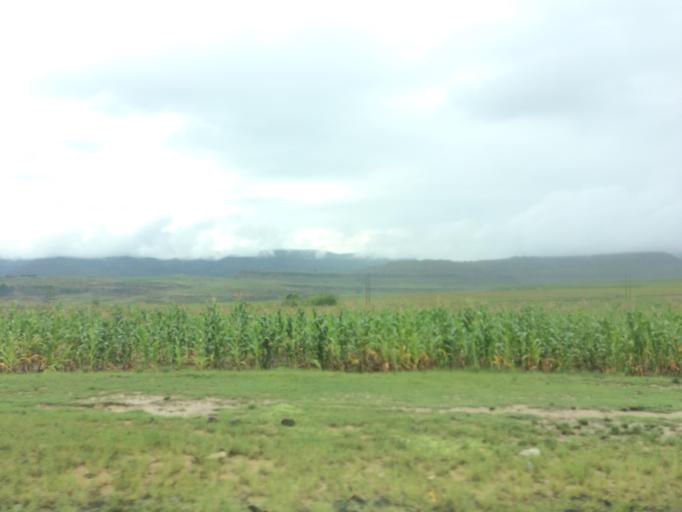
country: LS
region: Mafeteng
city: Mafeteng
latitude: -29.7183
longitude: 27.4859
